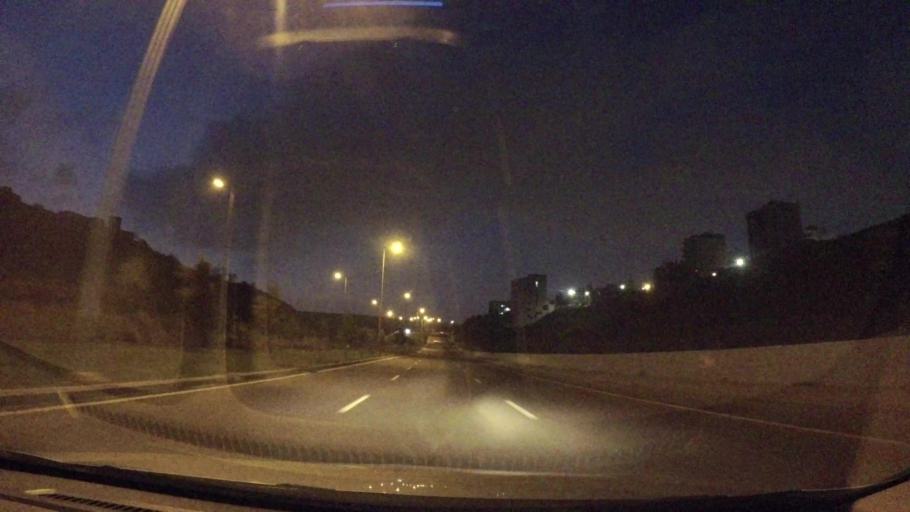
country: JO
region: Amman
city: Al Bunayyat ash Shamaliyah
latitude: 31.9203
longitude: 35.8798
